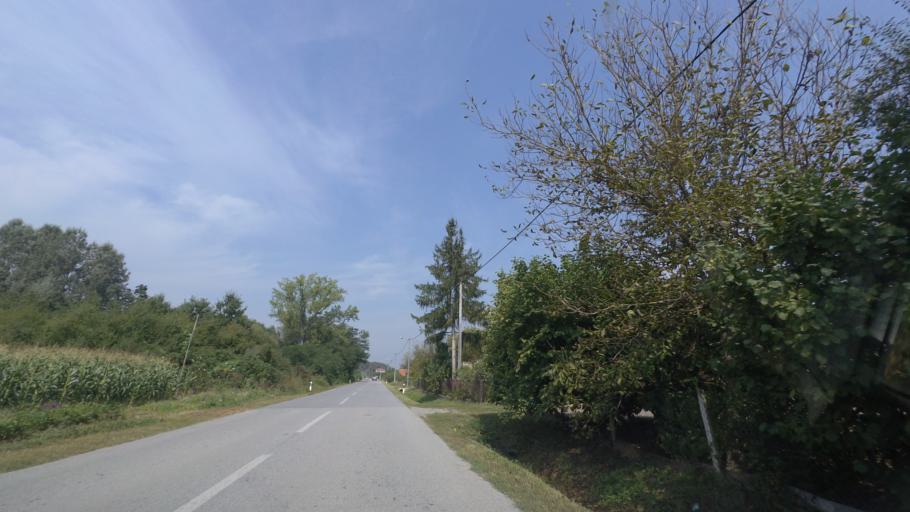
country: HR
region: Sisacko-Moslavacka
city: Glina
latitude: 45.2957
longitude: 16.1356
